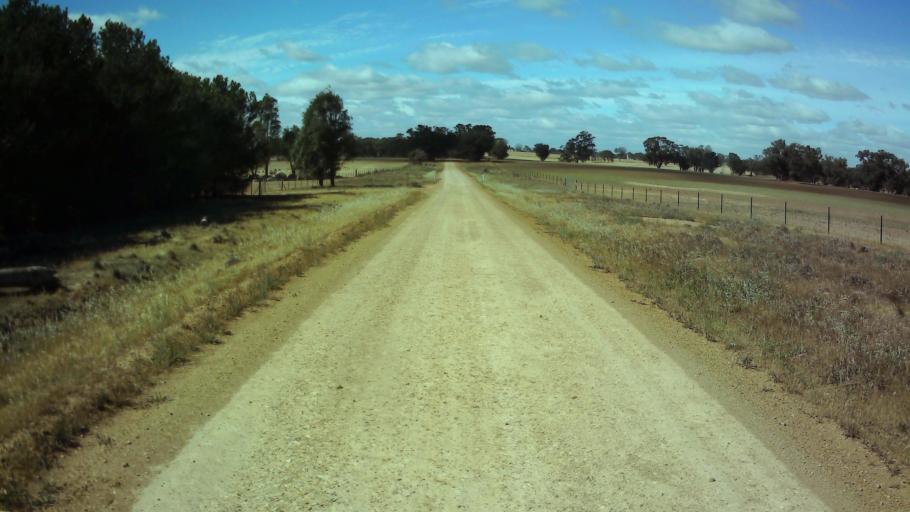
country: AU
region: New South Wales
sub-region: Weddin
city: Grenfell
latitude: -34.0602
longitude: 148.3122
